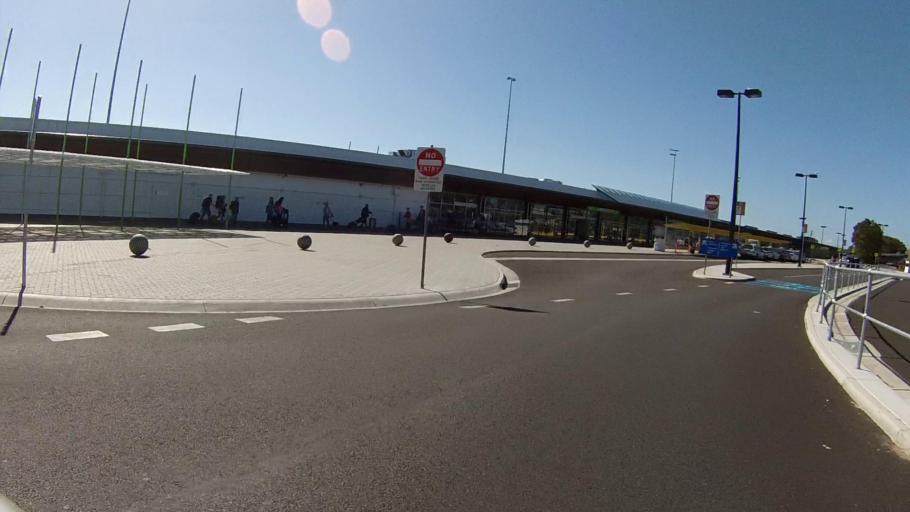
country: AU
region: Tasmania
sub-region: Clarence
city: Seven Mile Beach
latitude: -42.8365
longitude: 147.5037
